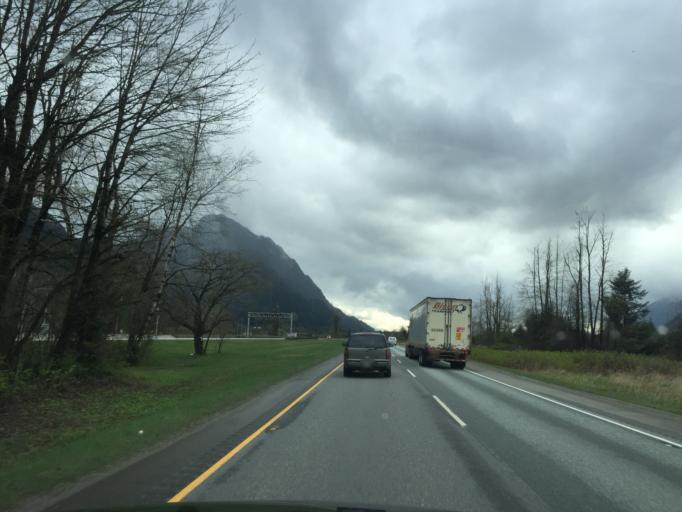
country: CA
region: British Columbia
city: Hope
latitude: 49.3335
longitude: -121.6084
